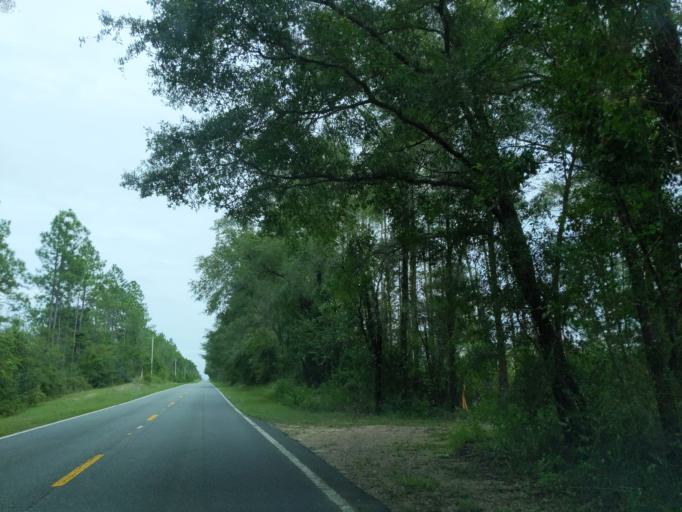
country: US
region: Florida
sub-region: Leon County
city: Woodville
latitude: 30.3766
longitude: -84.2188
